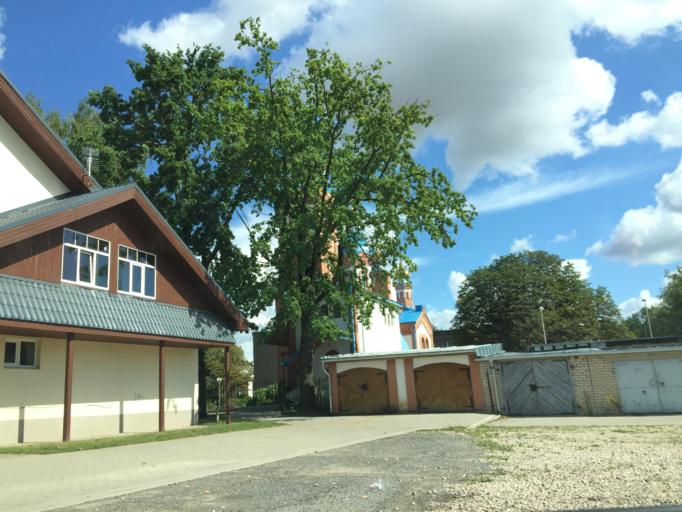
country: LV
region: Bauskas Rajons
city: Bauska
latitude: 56.4050
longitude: 24.1840
